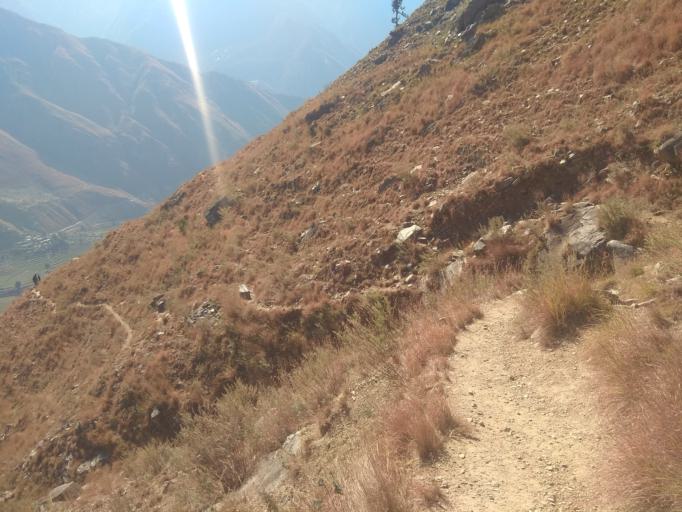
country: NP
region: Mid Western
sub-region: Karnali Zone
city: Jumla
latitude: 29.3108
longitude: 81.7468
